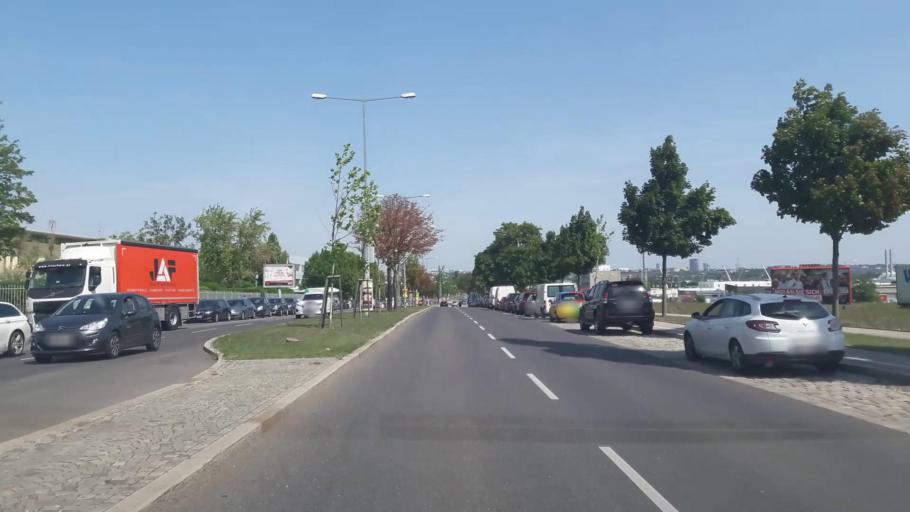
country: AT
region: Lower Austria
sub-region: Politischer Bezirk Modling
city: Vosendorf
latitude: 48.1323
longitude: 16.3555
